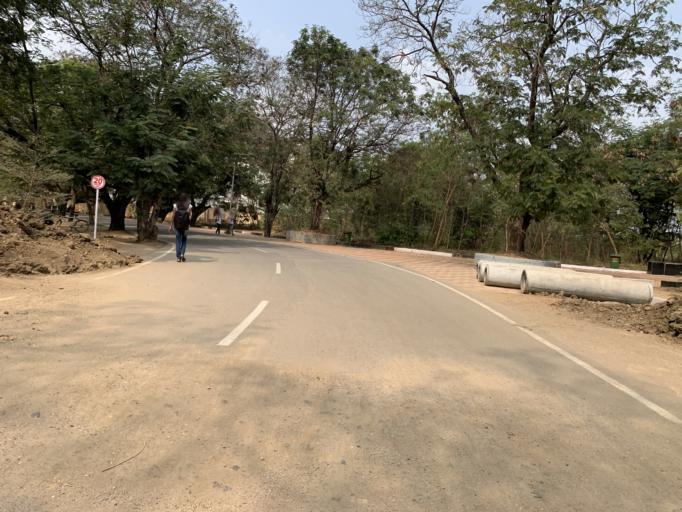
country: IN
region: Telangana
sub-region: Warangal
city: Warangal
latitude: 17.9842
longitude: 79.5321
